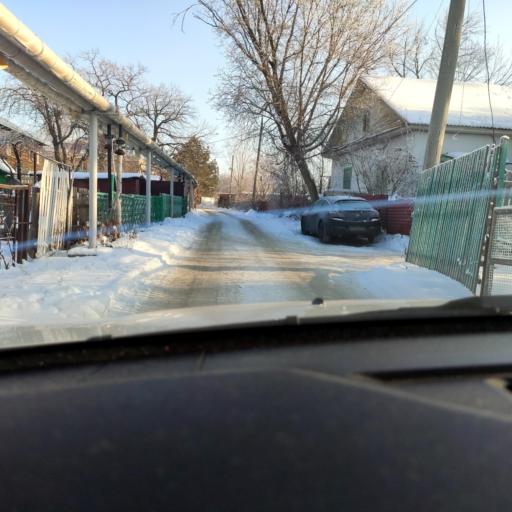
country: RU
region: Samara
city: Samara
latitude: 53.2552
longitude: 50.1856
